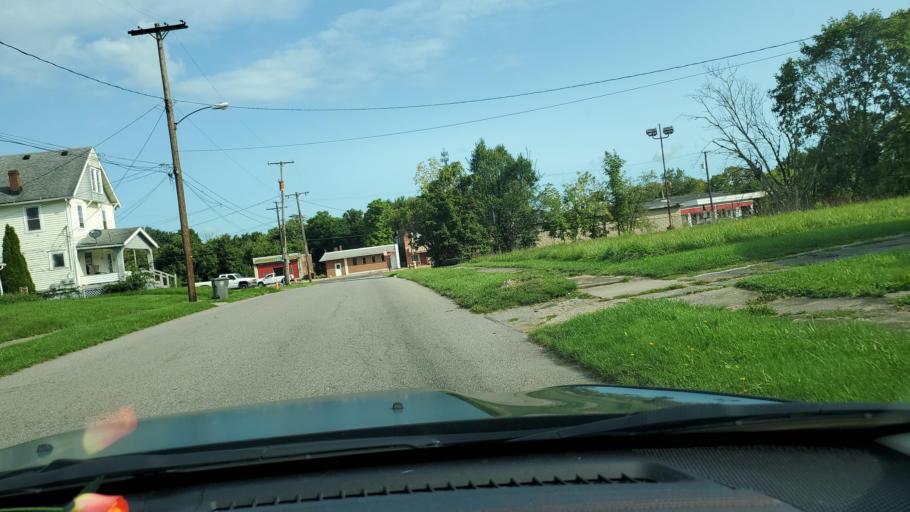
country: US
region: Ohio
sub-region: Mahoning County
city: Youngstown
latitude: 41.1009
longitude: -80.6811
